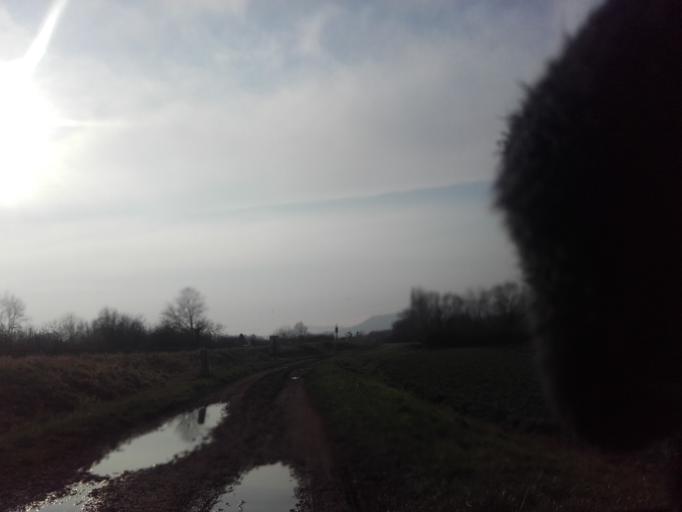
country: FR
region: Bourgogne
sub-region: Departement de Saone-et-Loire
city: Chagny
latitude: 46.9151
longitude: 4.7338
